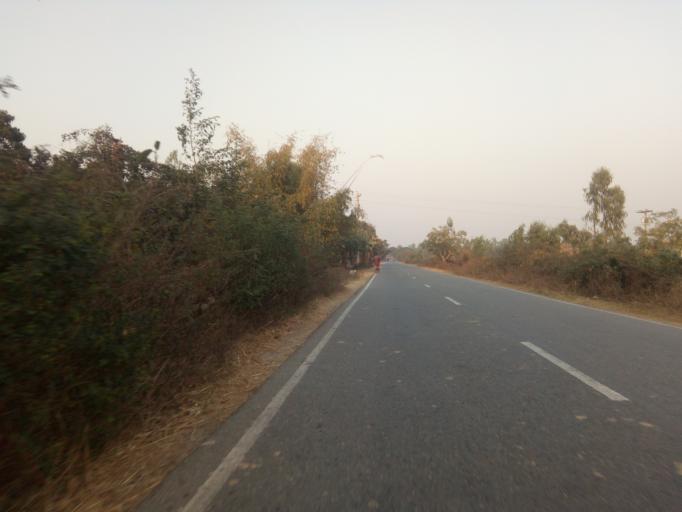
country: BD
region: Rajshahi
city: Bogra
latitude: 24.5881
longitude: 89.2322
